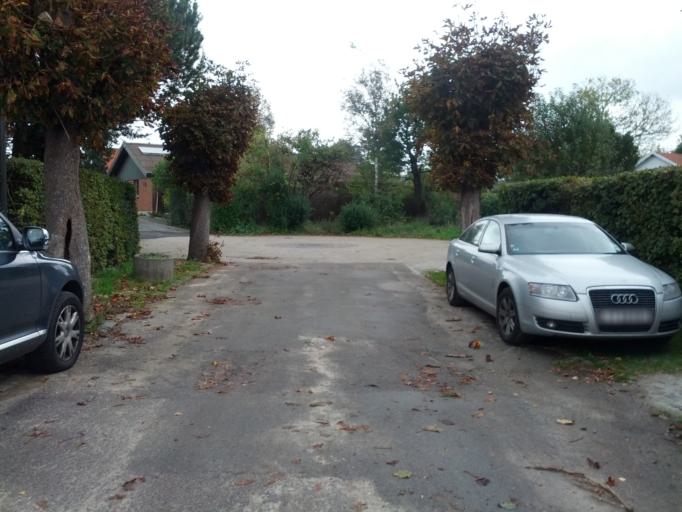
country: DK
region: Capital Region
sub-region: Herlev Kommune
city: Herlev
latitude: 55.7225
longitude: 12.4457
